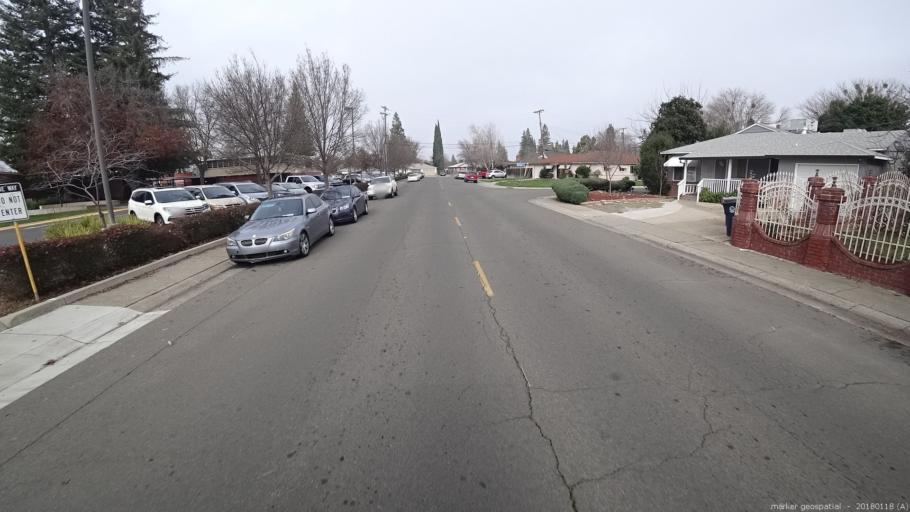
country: US
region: California
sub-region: Sacramento County
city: Rancho Cordova
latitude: 38.5965
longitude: -121.3092
